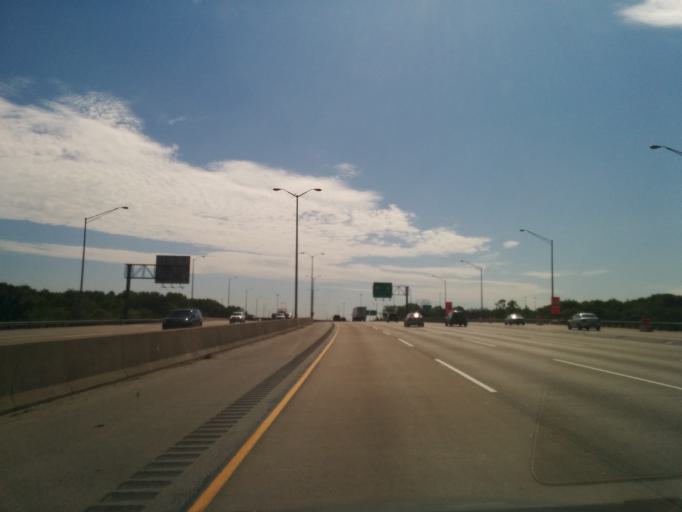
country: US
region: Illinois
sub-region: Cook County
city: Thornton
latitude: 41.5777
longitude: -87.5918
